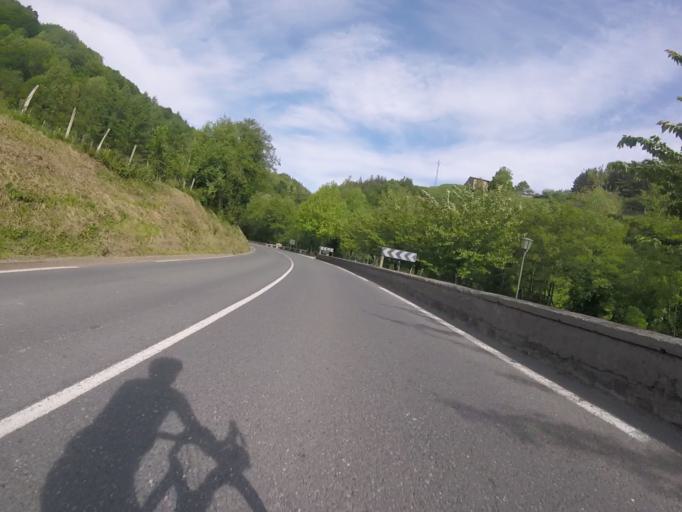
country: ES
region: Basque Country
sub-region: Provincia de Guipuzcoa
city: Urretxu
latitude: 43.1082
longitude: -2.3179
